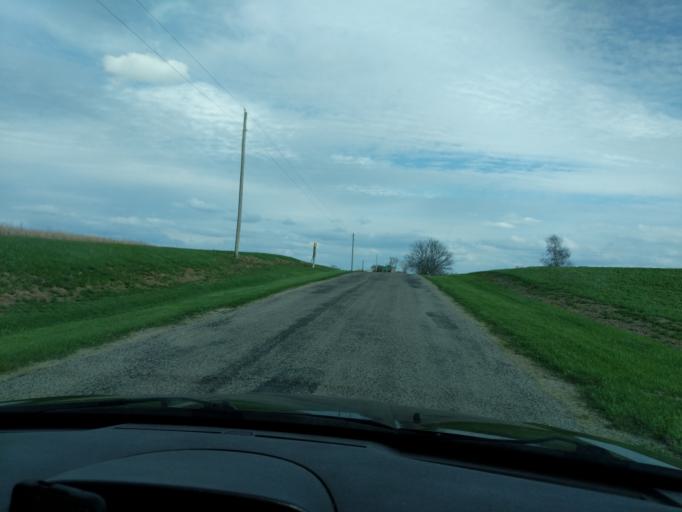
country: US
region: Ohio
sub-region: Champaign County
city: North Lewisburg
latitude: 40.1963
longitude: -83.6559
